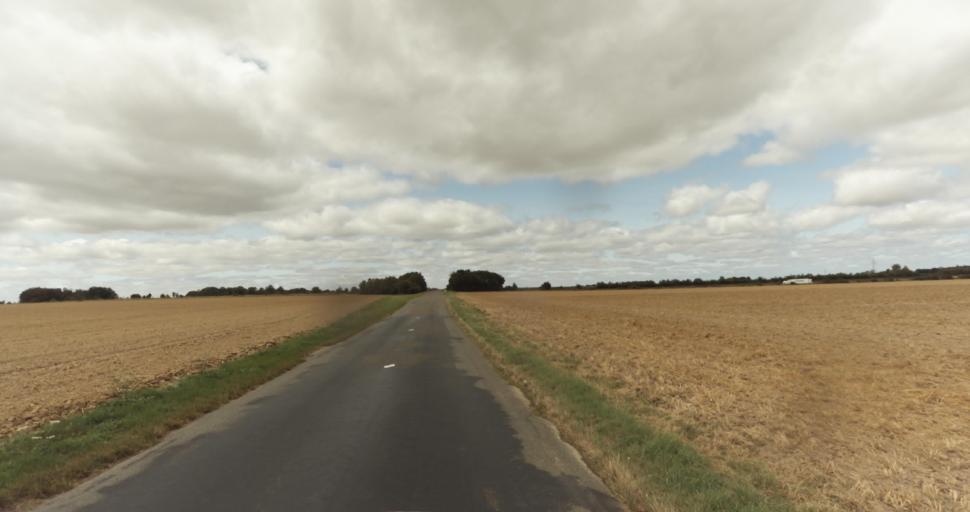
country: FR
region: Haute-Normandie
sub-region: Departement de l'Eure
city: Evreux
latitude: 48.9167
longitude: 1.2005
